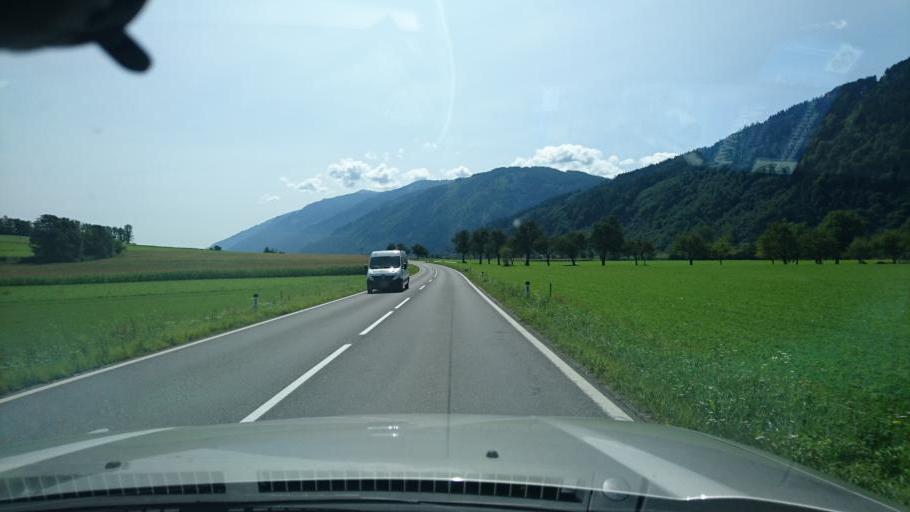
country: AT
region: Carinthia
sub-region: Politischer Bezirk Spittal an der Drau
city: Muhldorf
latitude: 46.8541
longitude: 13.3542
